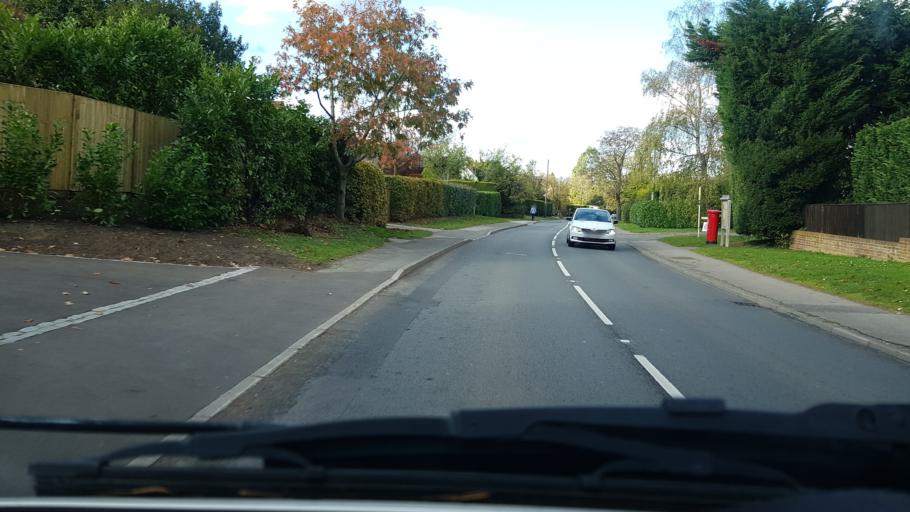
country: GB
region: England
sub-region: Surrey
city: Send
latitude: 51.2646
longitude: -0.5049
